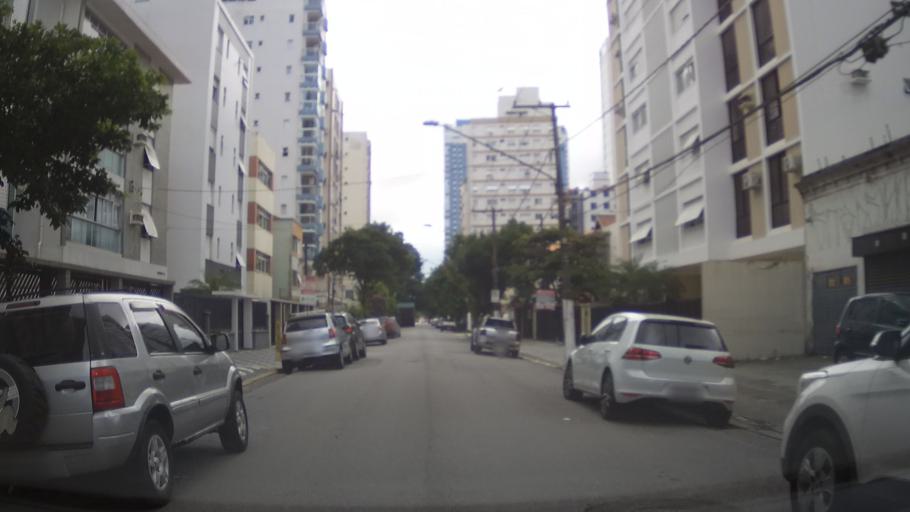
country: BR
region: Sao Paulo
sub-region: Santos
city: Santos
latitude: -23.9827
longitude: -46.3094
